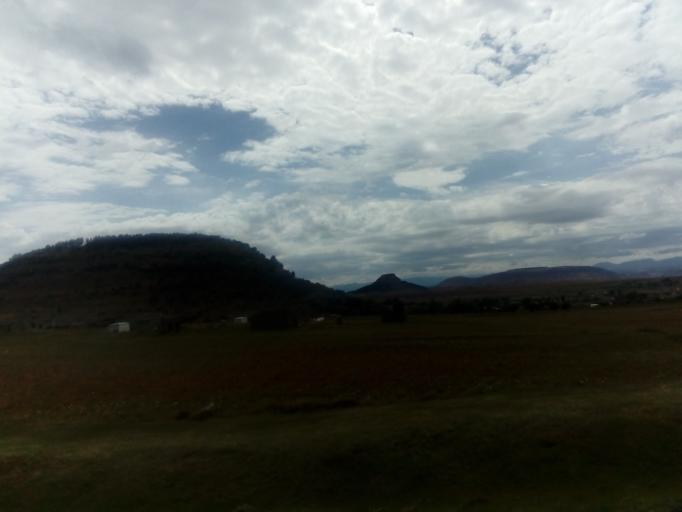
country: LS
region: Leribe
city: Maputsoe
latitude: -28.9564
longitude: 27.9610
